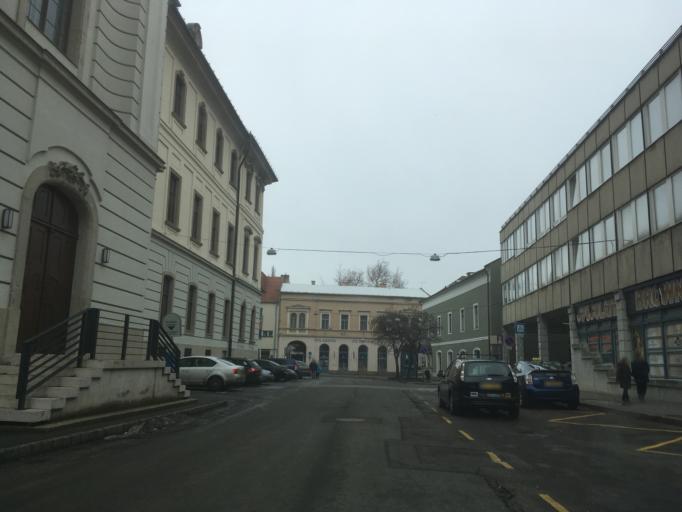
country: HU
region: Heves
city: Eger
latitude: 47.9001
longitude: 20.3765
